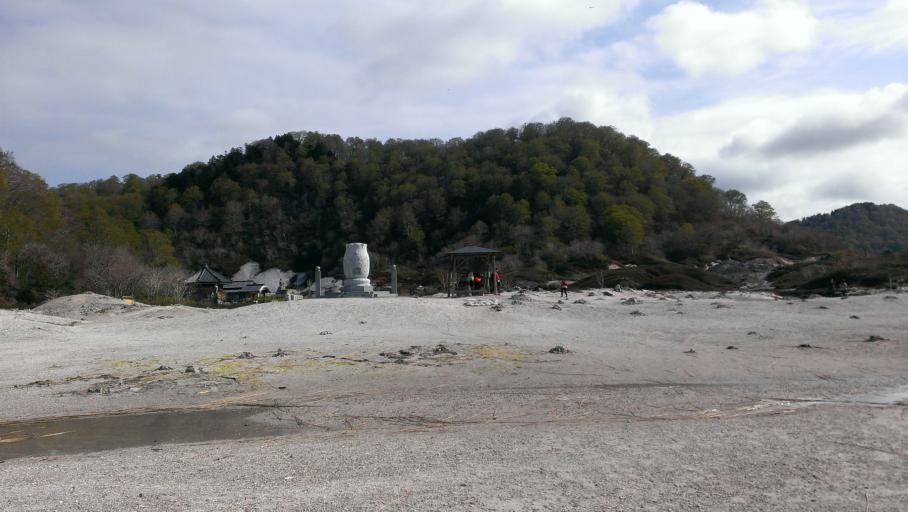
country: JP
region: Aomori
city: Mutsu
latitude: 41.3266
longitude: 141.0850
